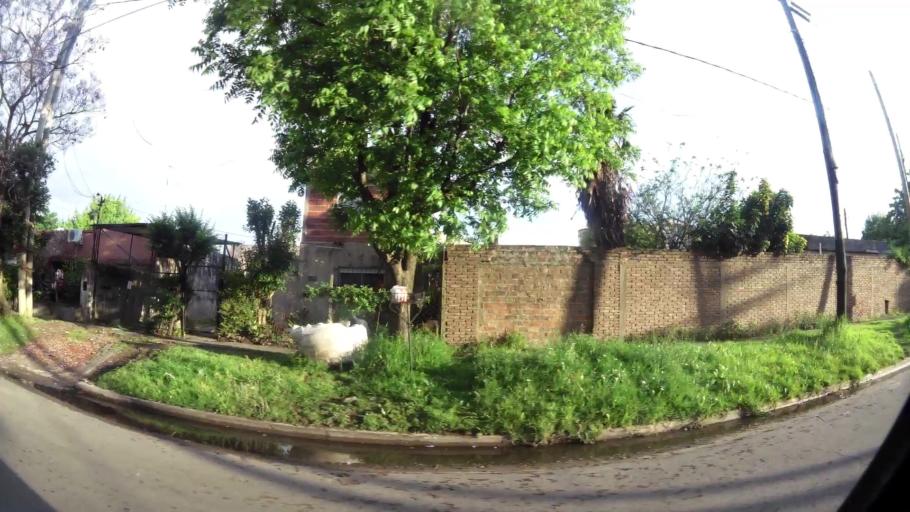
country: AR
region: Buenos Aires
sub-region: Partido de Lomas de Zamora
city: Lomas de Zamora
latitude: -34.7578
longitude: -58.3626
